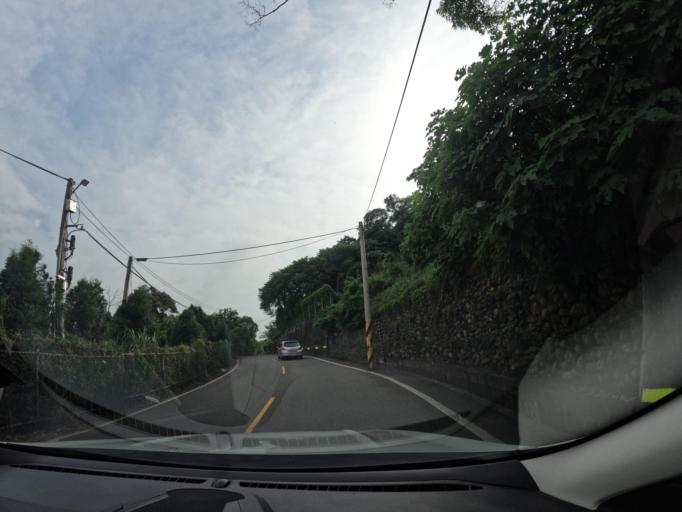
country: TW
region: Taiwan
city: Daxi
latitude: 24.9282
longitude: 121.3050
